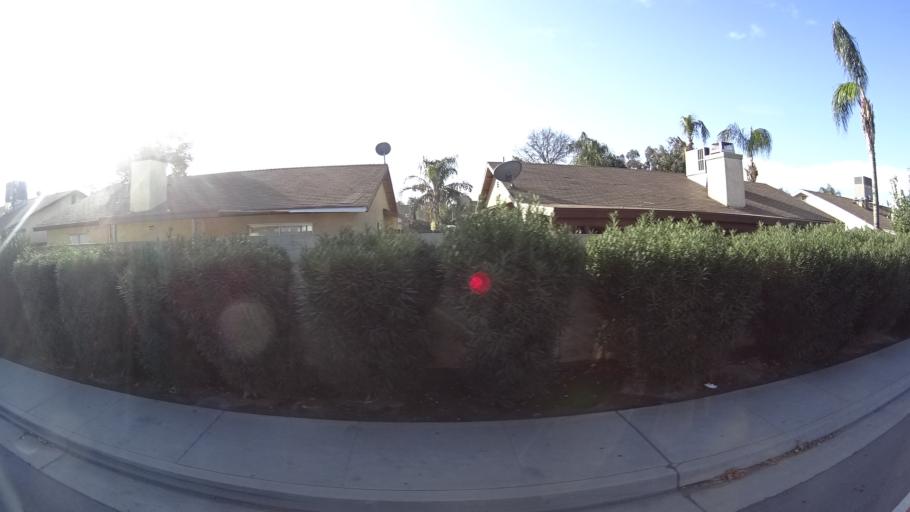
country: US
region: California
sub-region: Kern County
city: Greenfield
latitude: 35.3031
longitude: -119.0544
